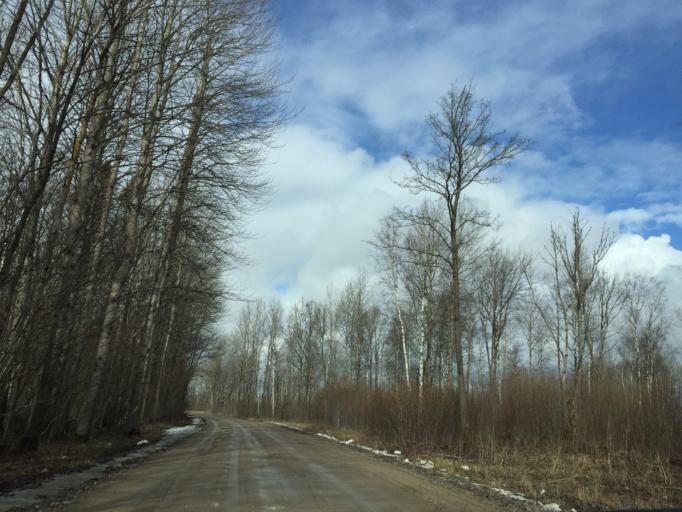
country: EE
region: Laeaene
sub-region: Lihula vald
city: Lihula
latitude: 58.7310
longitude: 23.8312
